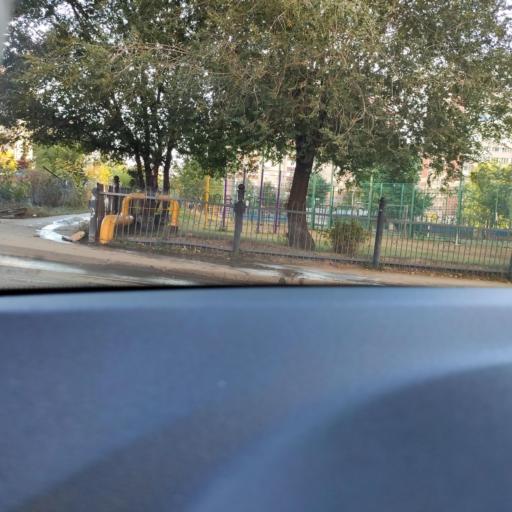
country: RU
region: Samara
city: Samara
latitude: 53.2164
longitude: 50.1669
